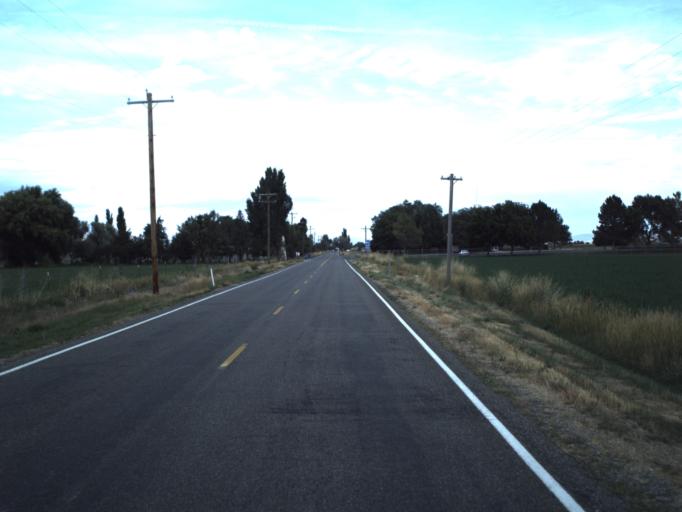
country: US
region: Utah
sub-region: Cache County
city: Lewiston
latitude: 41.9359
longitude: -111.9534
